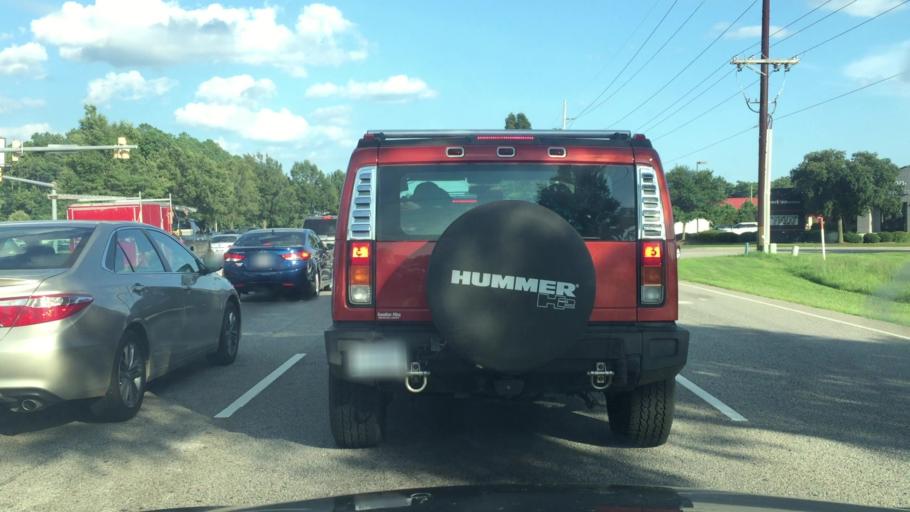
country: US
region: South Carolina
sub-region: Horry County
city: Myrtle Beach
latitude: 33.7068
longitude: -78.9112
